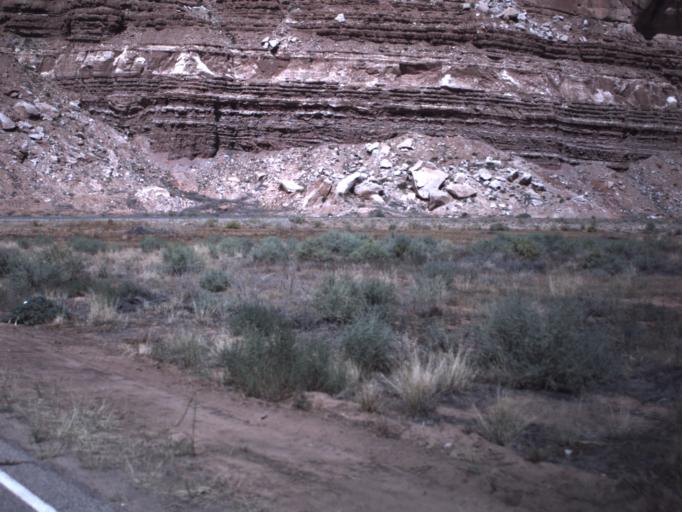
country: US
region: Utah
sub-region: San Juan County
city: Blanding
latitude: 37.2862
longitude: -109.5443
